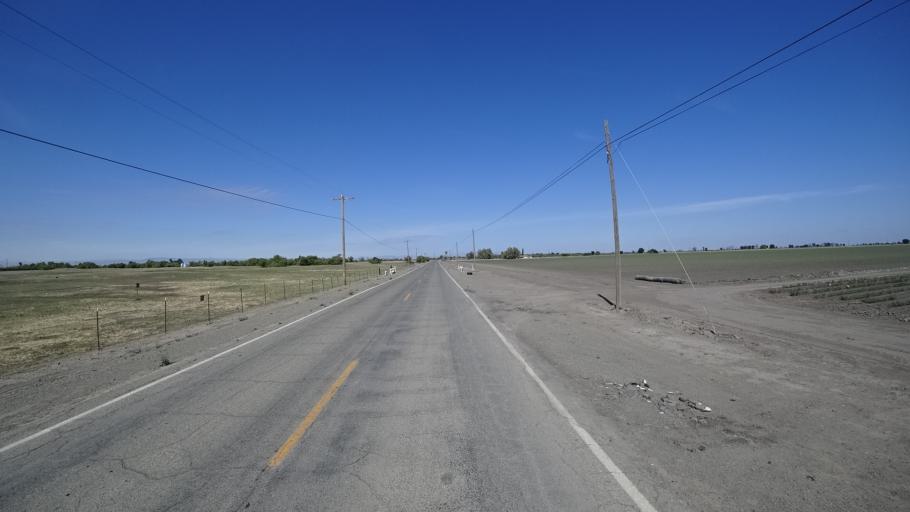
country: US
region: California
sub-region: Kings County
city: Lemoore Station
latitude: 36.2554
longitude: -119.8453
